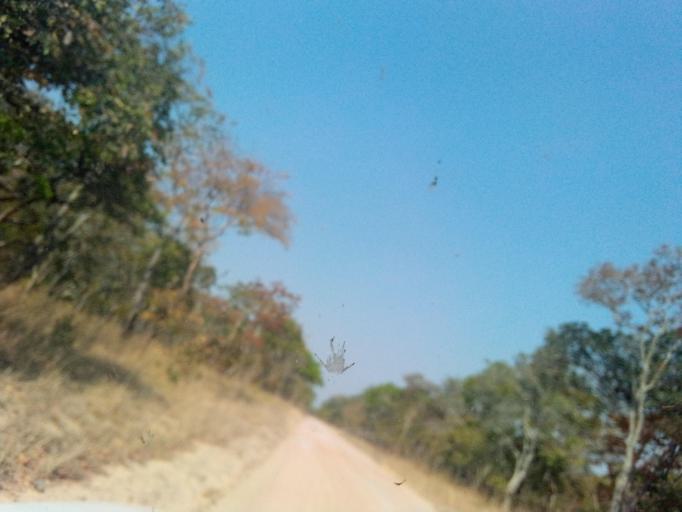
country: ZM
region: Northern
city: Mpika
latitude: -12.2252
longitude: 30.8950
